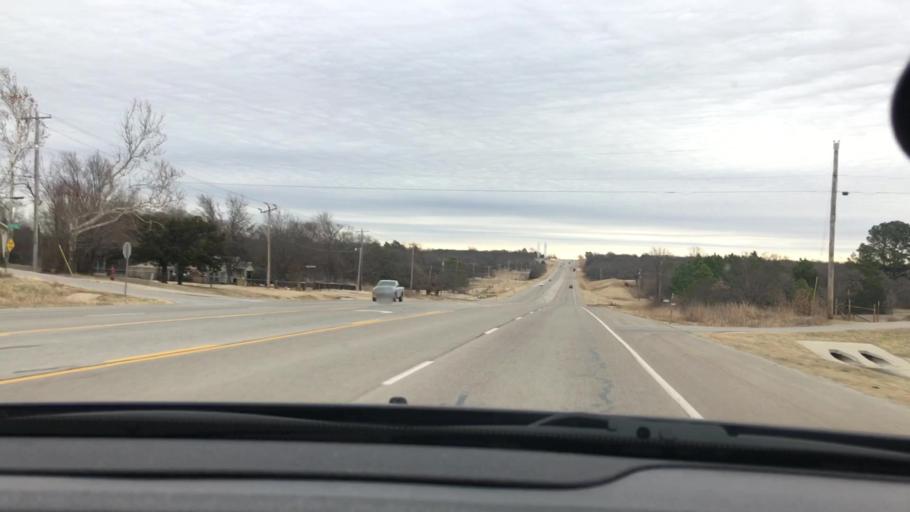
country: US
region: Oklahoma
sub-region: Carter County
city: Dickson
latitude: 34.1871
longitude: -97.0171
